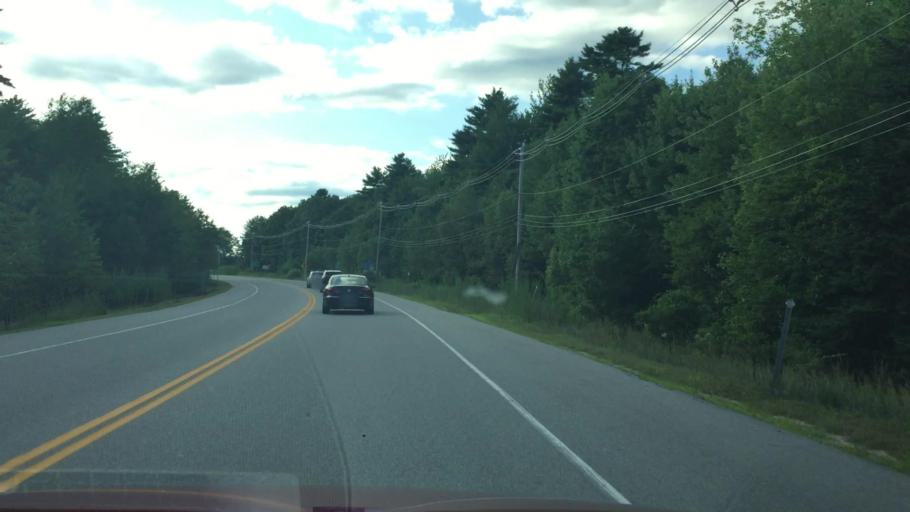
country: US
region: Maine
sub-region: Cumberland County
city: West Scarborough
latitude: 43.6014
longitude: -70.3634
